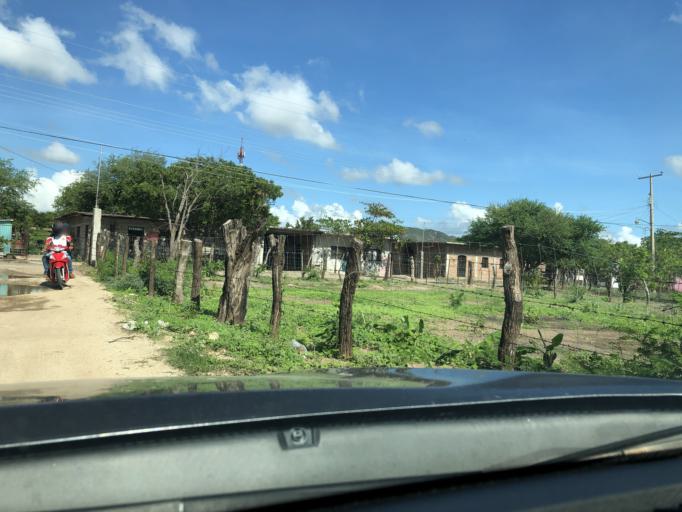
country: MX
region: Oaxaca
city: San Jeronimo Ixtepec
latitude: 16.5524
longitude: -95.1054
